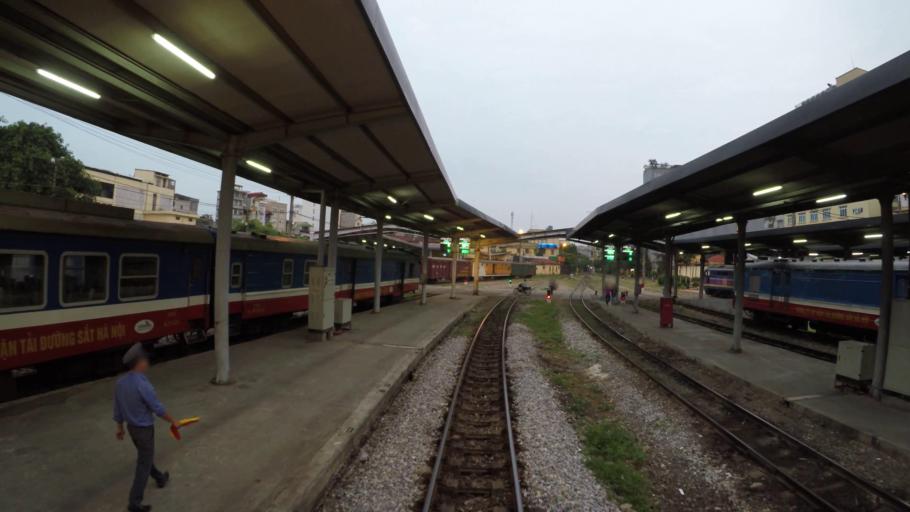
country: VN
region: Ha Noi
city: Hanoi
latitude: 21.0274
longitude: 105.8412
